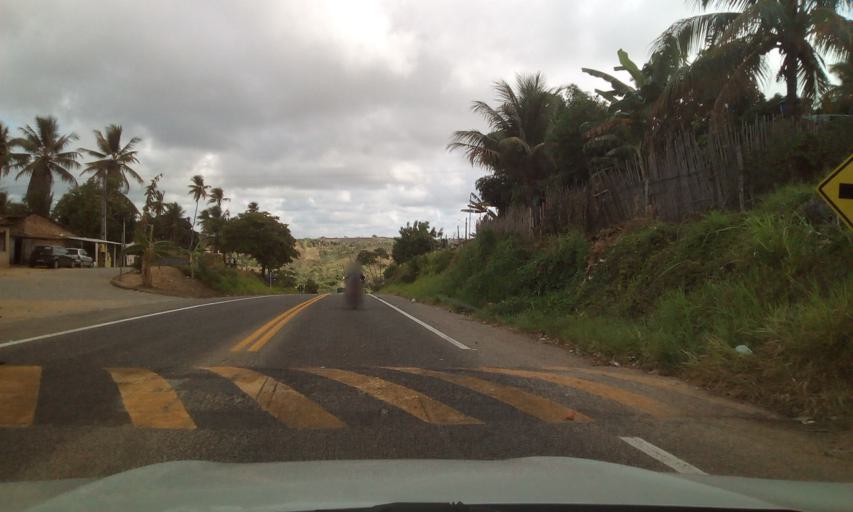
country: BR
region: Sergipe
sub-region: Indiaroba
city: Indiaroba
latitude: -11.5452
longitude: -37.5697
